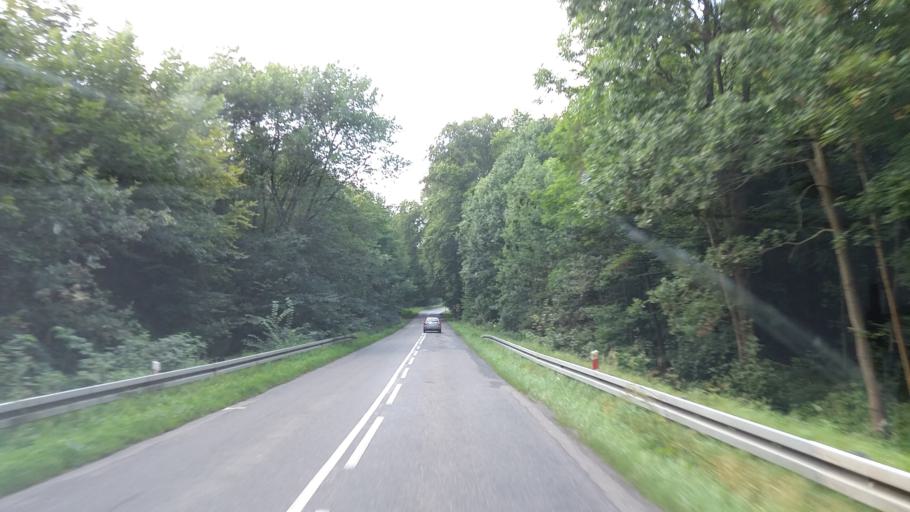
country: PL
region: West Pomeranian Voivodeship
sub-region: Powiat choszczenski
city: Pelczyce
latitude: 53.0820
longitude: 15.2843
